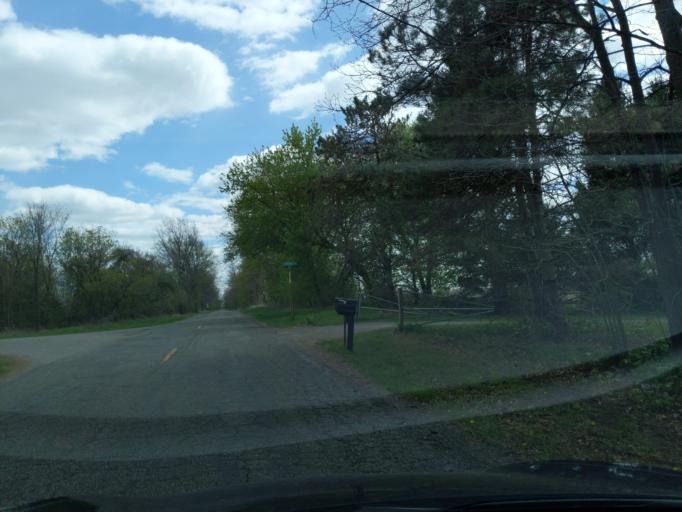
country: US
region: Michigan
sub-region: Ingham County
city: Leslie
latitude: 42.4803
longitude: -84.5412
